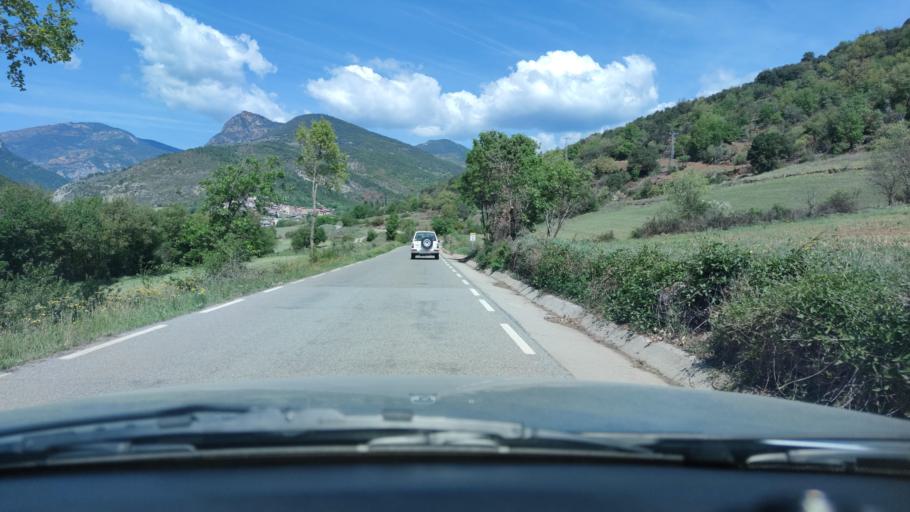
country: ES
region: Catalonia
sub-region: Provincia de Lleida
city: Coll de Nargo
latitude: 42.2899
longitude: 1.3577
